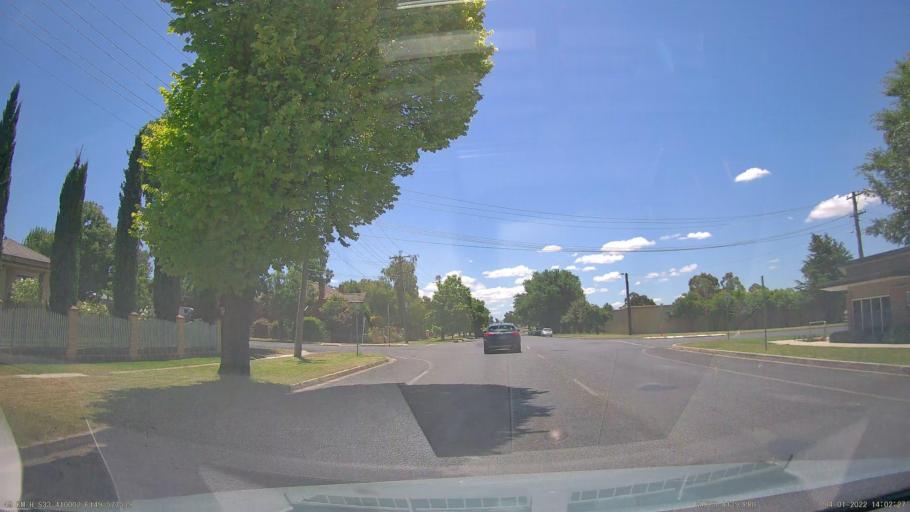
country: AU
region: New South Wales
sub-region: Bathurst Regional
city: Bathurst
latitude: -33.4099
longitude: 149.5774
